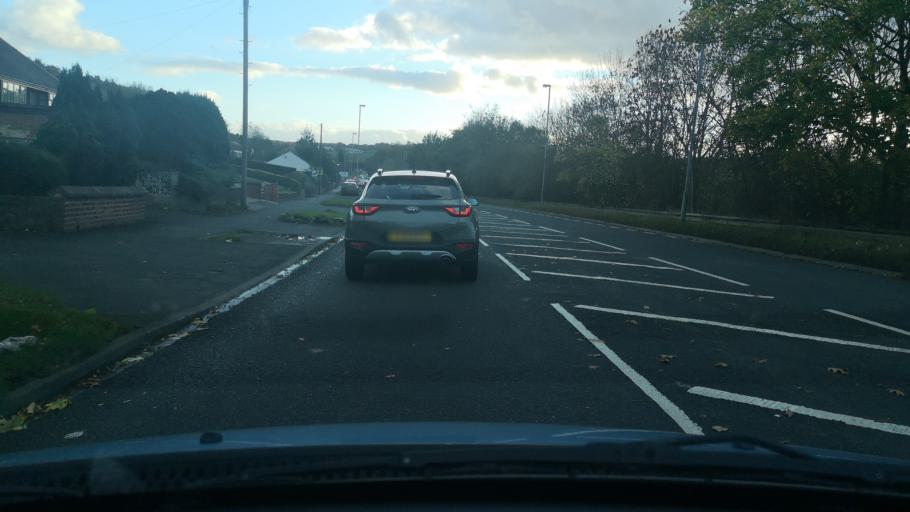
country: GB
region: England
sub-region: City and Borough of Wakefield
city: Crigglestone
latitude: 53.6444
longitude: -1.5462
